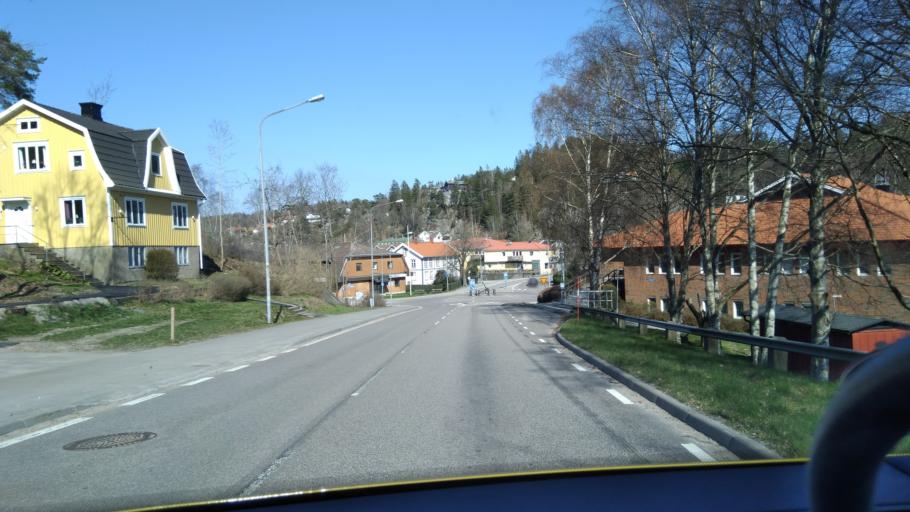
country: SE
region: Vaestra Goetaland
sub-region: Orust
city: Henan
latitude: 58.2354
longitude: 11.6775
